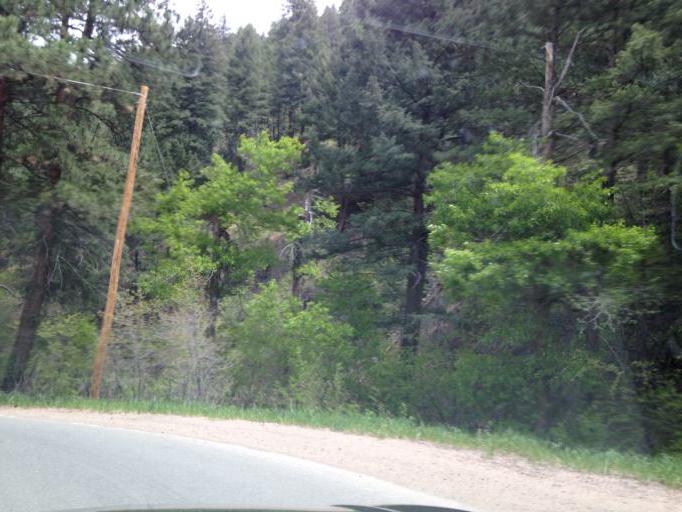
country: US
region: Colorado
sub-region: Jefferson County
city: Ken Caryl
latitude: 39.5046
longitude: -105.1868
